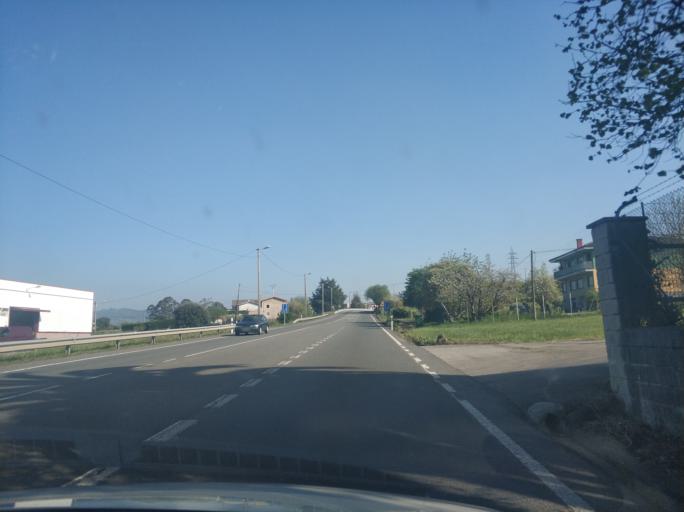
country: ES
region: Cantabria
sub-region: Provincia de Cantabria
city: Colindres
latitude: 43.3995
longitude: -3.4781
